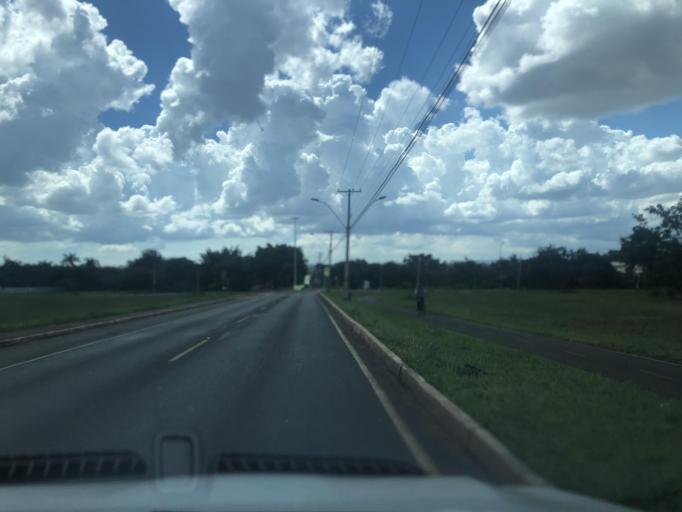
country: BR
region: Federal District
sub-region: Brasilia
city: Brasilia
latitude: -15.8971
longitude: -47.9299
